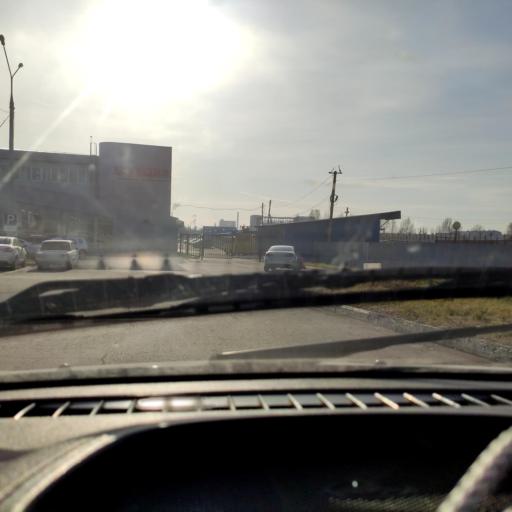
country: RU
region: Samara
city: Tol'yatti
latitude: 53.5712
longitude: 49.4686
